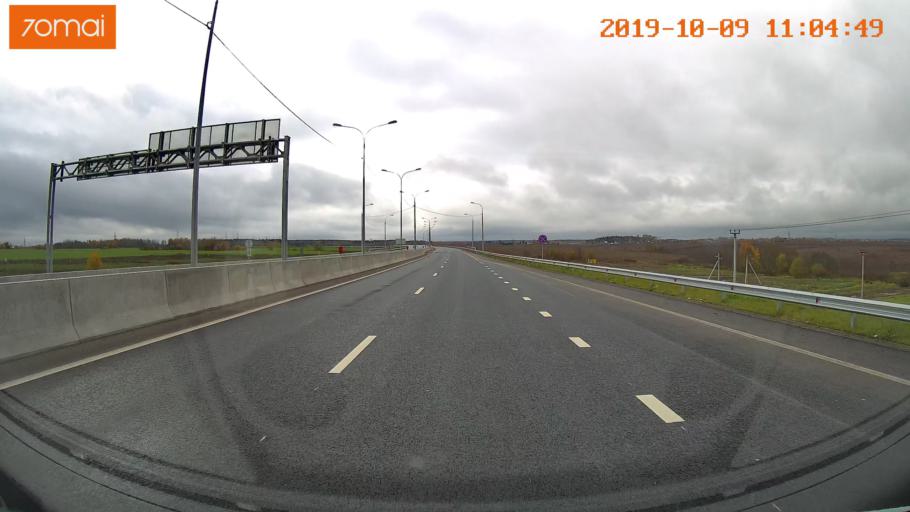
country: RU
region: Vologda
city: Molochnoye
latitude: 59.2076
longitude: 39.7631
